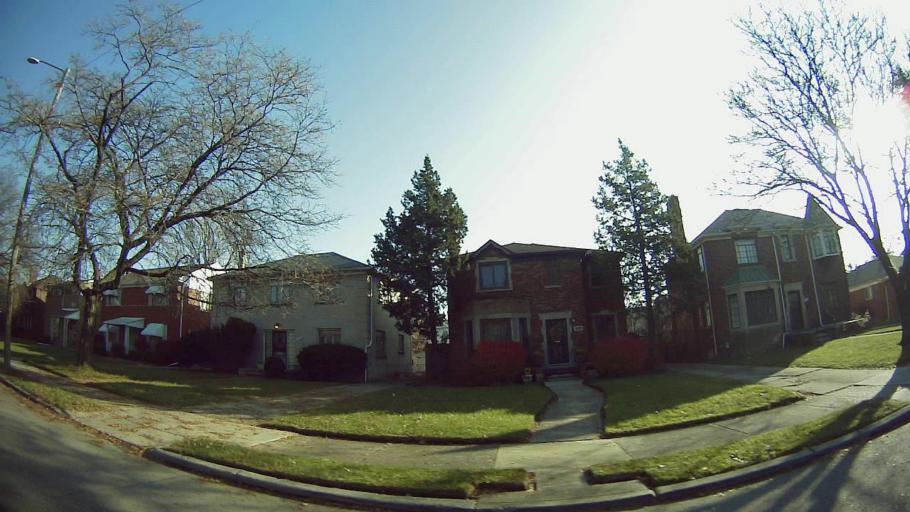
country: US
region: Michigan
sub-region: Wayne County
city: Highland Park
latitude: 42.3819
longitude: -83.1437
